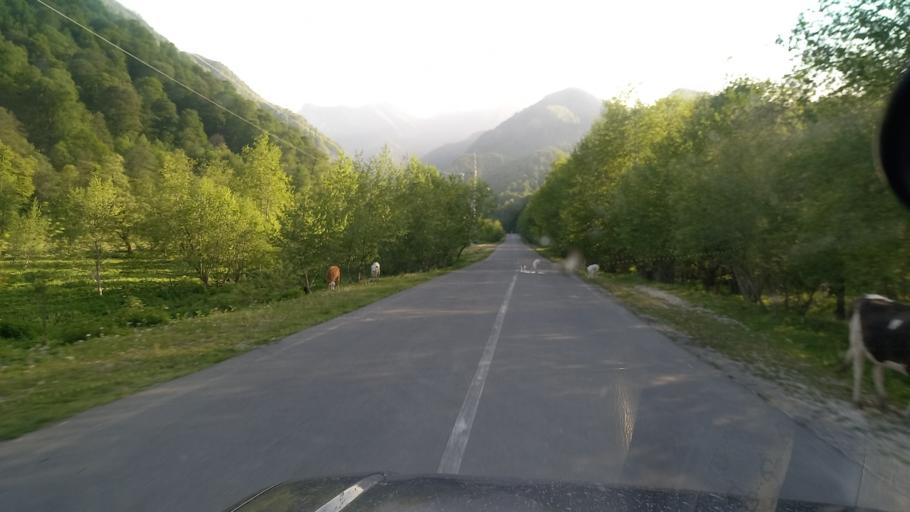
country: RU
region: North Ossetia
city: Tarskoye
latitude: 42.9061
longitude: 44.9584
